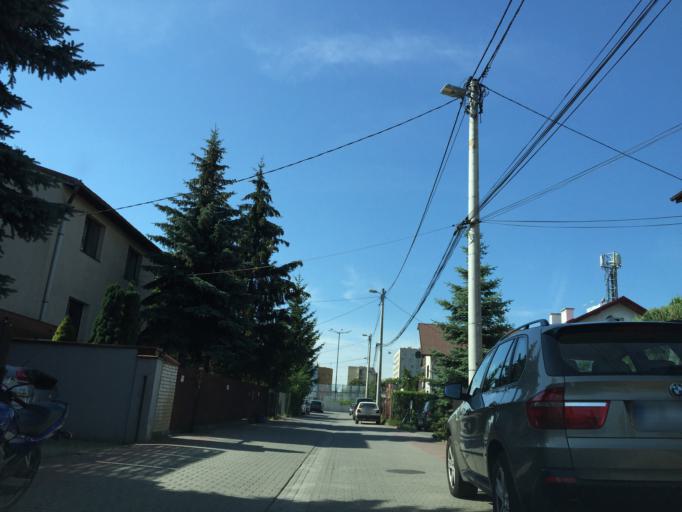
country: PL
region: Lesser Poland Voivodeship
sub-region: Powiat krakowski
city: Zielonki
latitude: 50.0906
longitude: 19.9127
